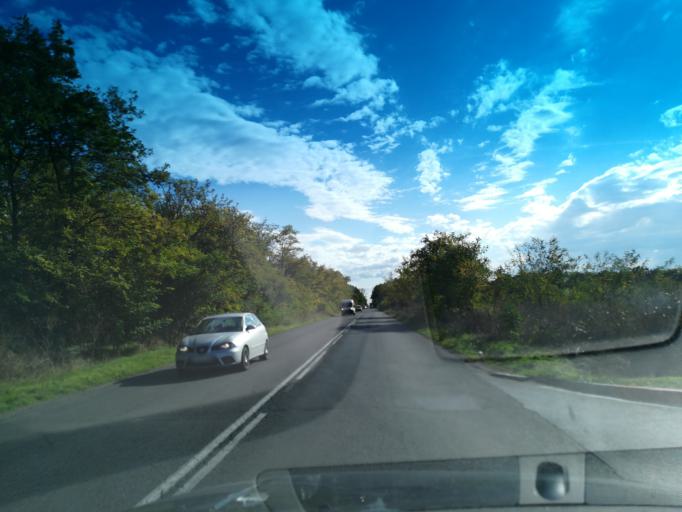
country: BG
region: Stara Zagora
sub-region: Obshtina Stara Zagora
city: Stara Zagora
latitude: 42.3560
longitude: 25.6572
